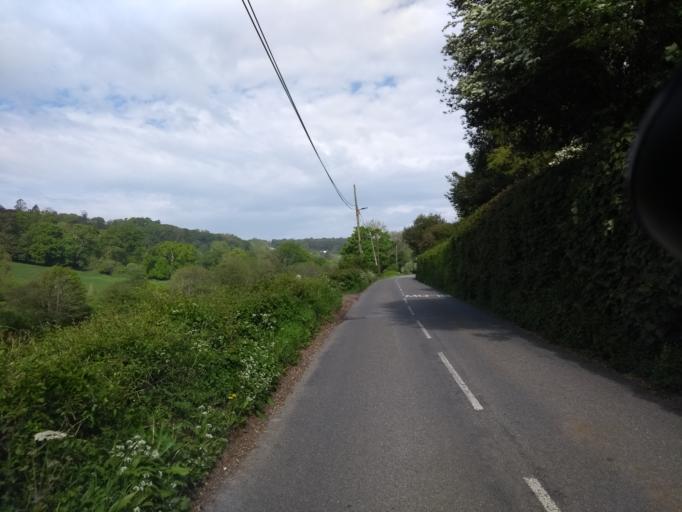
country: GB
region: England
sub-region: Dorset
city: Lyme Regis
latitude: 50.7379
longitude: -2.9612
